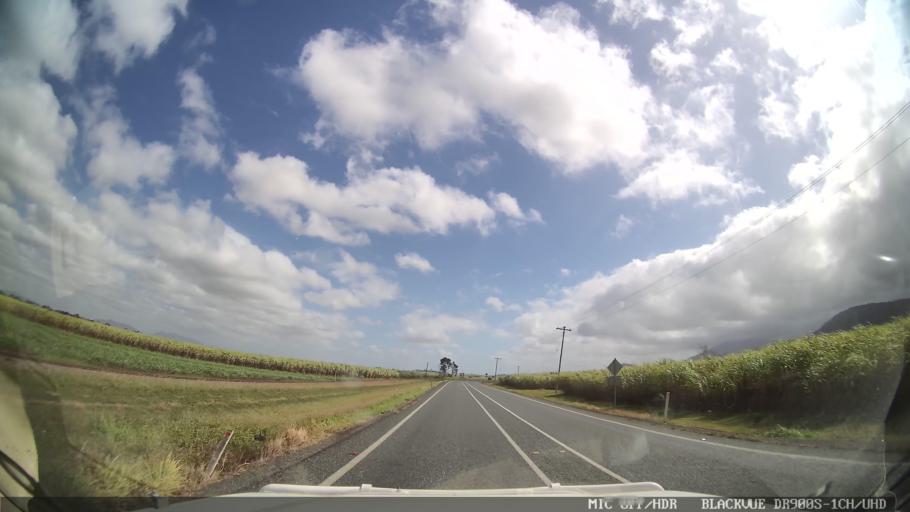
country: AU
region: Queensland
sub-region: Whitsunday
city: Proserpine
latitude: -20.3486
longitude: 148.5547
